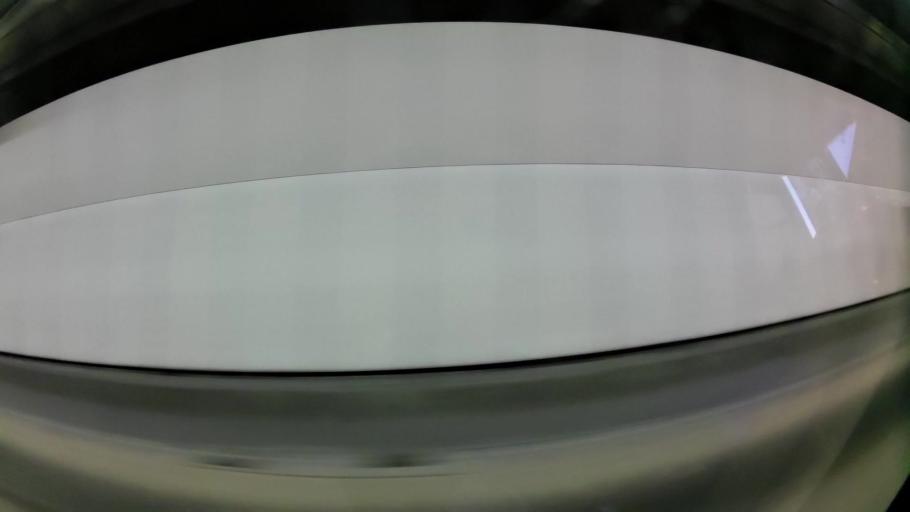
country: HK
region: Sha Tin
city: Sha Tin
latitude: 22.3801
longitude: 114.1641
